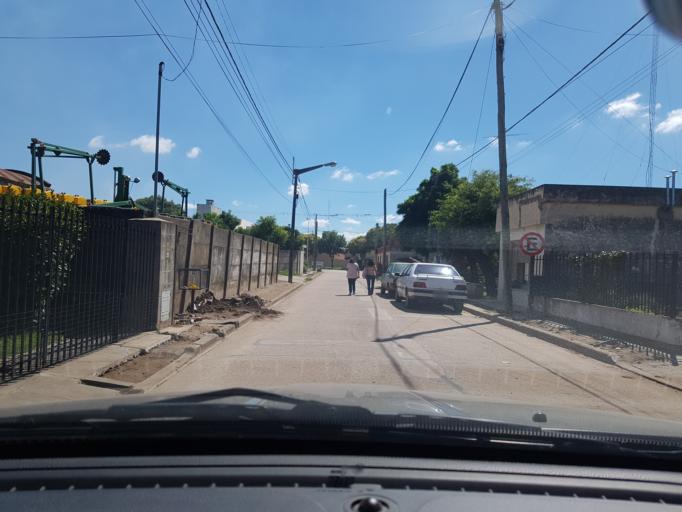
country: AR
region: Cordoba
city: General Cabrera
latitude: -32.7599
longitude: -63.7928
